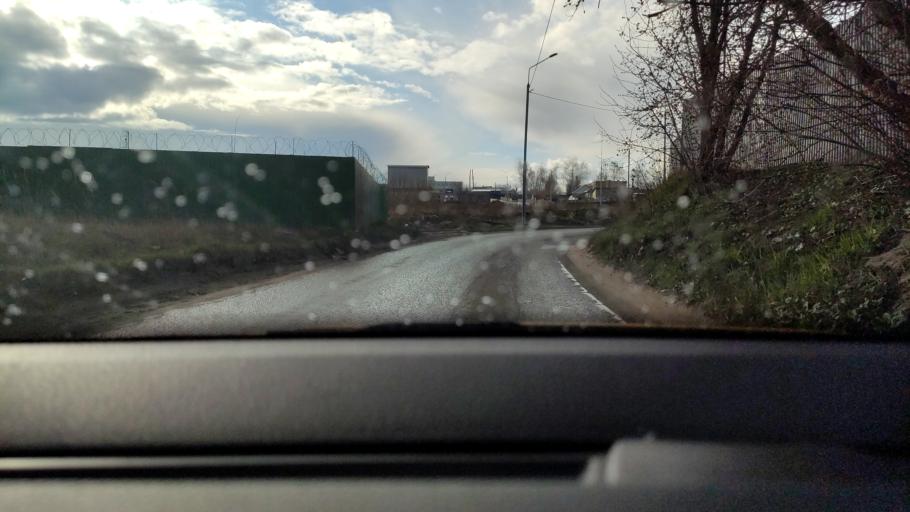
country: RU
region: Moskovskaya
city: Saltykovka
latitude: 55.7435
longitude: 37.9558
